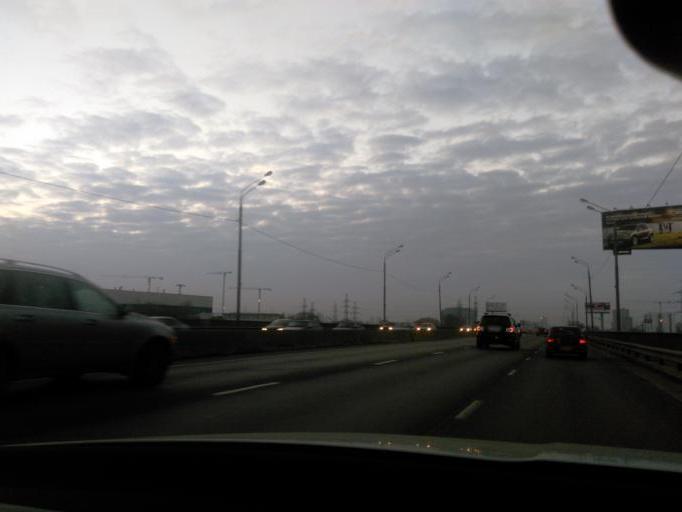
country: RU
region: Moscow
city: Khimki
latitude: 55.9180
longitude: 37.3963
